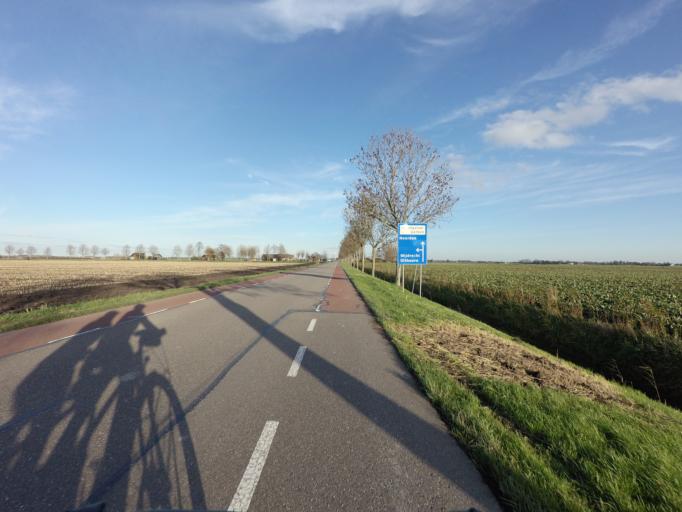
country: NL
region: South Holland
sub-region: Gemeente Nieuwkoop
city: Nieuwkoop
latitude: 52.1821
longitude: 4.7914
